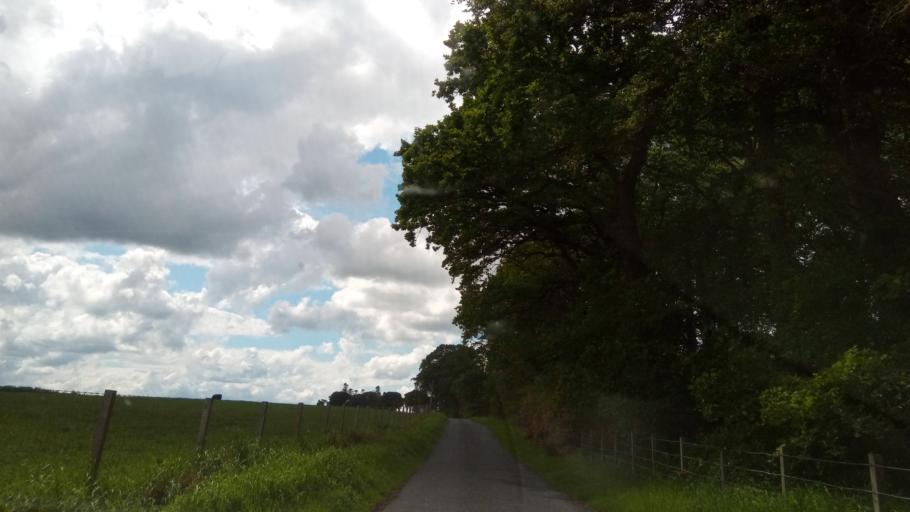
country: GB
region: Scotland
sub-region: The Scottish Borders
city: Coldstream
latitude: 55.5901
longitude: -2.2937
